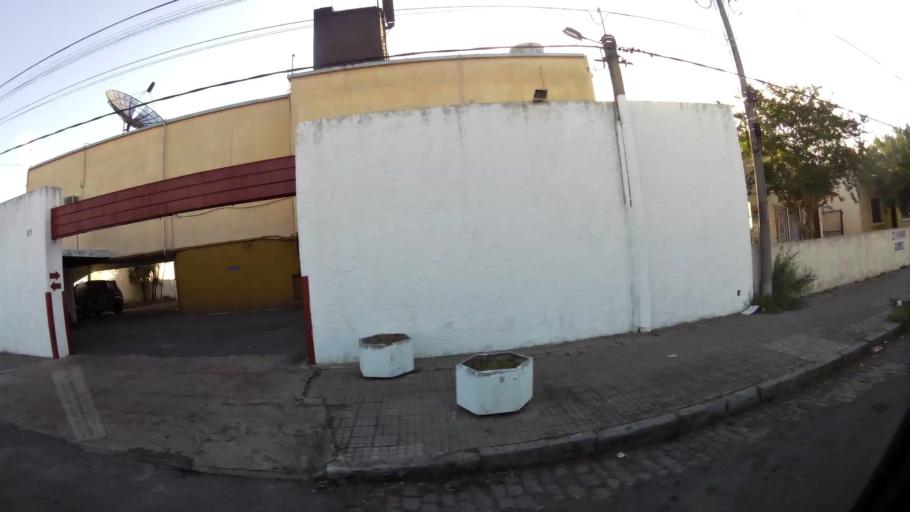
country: UY
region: Montevideo
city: Montevideo
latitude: -34.8704
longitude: -56.1459
